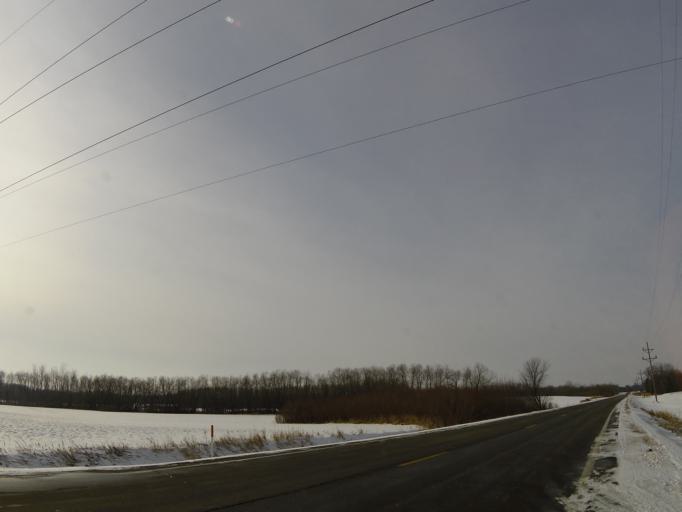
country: US
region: Minnesota
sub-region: McLeod County
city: Lester Prairie
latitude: 44.8765
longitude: -93.9909
